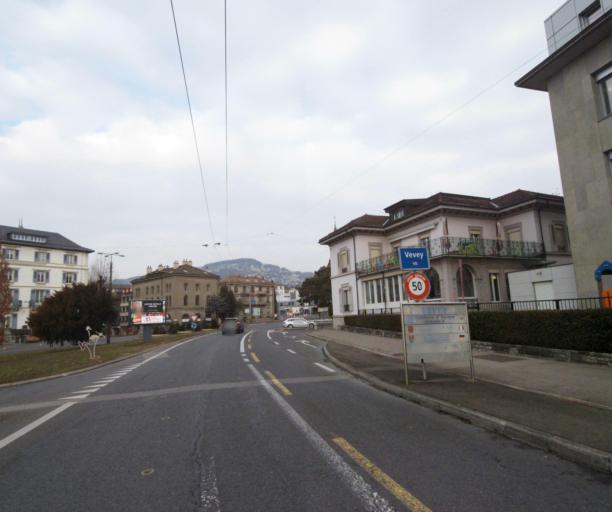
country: CH
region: Vaud
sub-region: Riviera-Pays-d'Enhaut District
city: La Tour-de-Peilz
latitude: 46.4571
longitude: 6.8531
